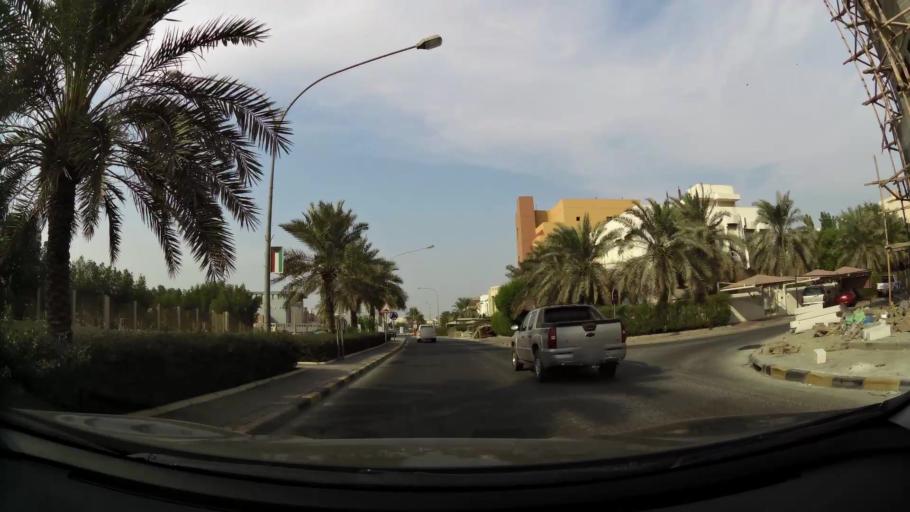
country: KW
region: Al Farwaniyah
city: Janub as Surrah
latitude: 29.3094
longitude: 47.9890
